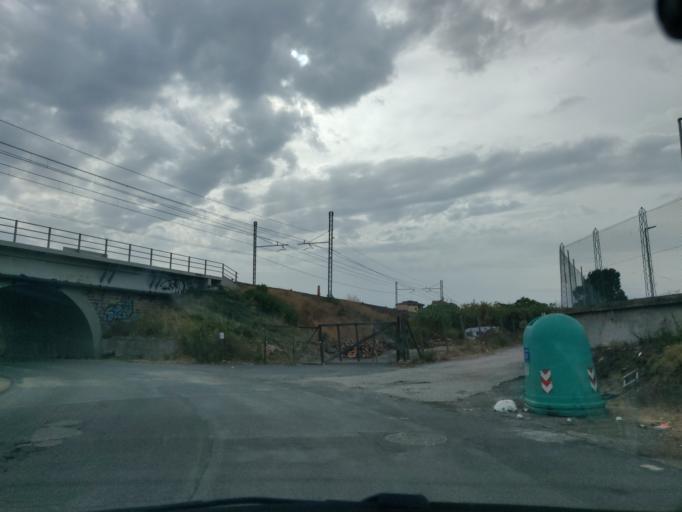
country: IT
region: Latium
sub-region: Citta metropolitana di Roma Capitale
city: Santa Marinella
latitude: 42.0412
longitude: 11.8926
